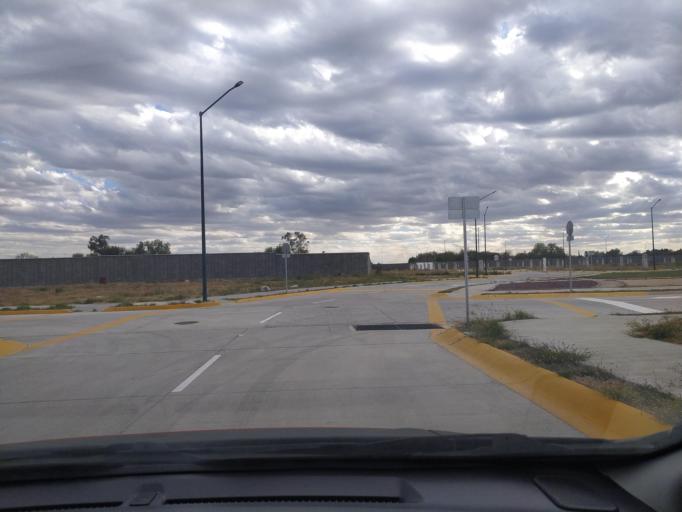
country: LA
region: Oudomxai
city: Muang La
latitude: 21.0247
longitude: 101.8221
